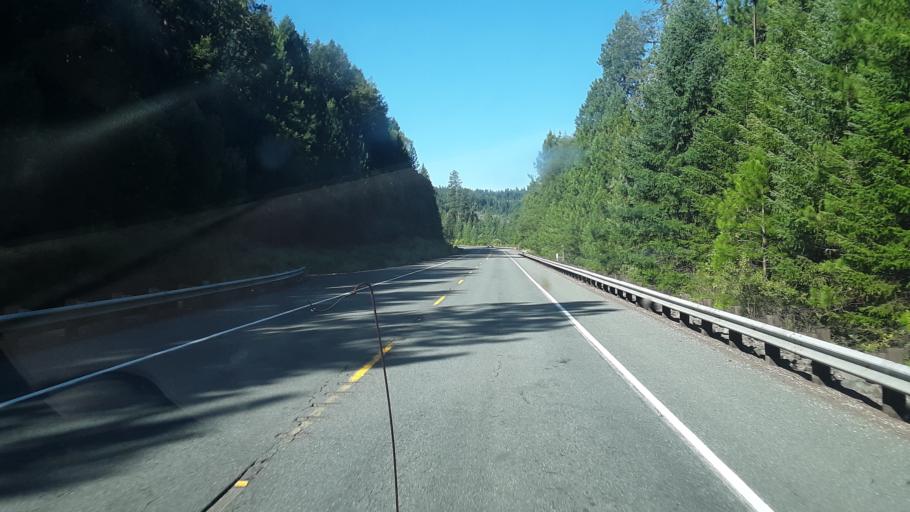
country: US
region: Oregon
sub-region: Jackson County
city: Shady Cove
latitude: 42.6709
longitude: -122.6393
